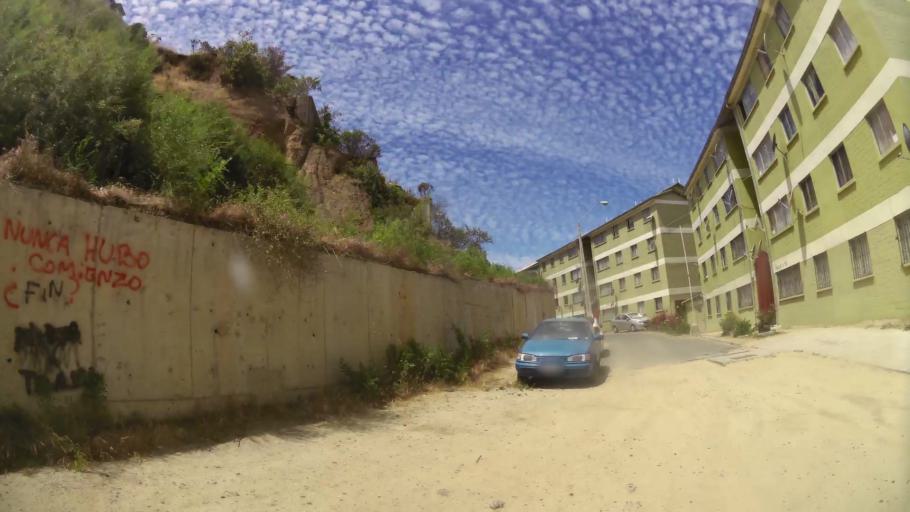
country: CL
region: Valparaiso
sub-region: Provincia de Valparaiso
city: Vina del Mar
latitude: -33.0604
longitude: -71.5622
